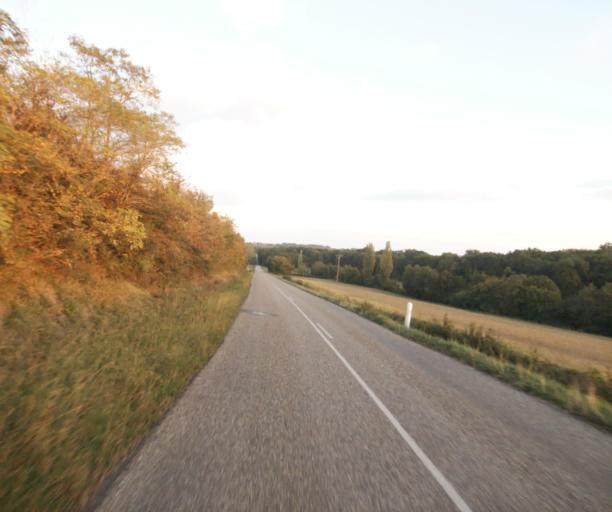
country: FR
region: Midi-Pyrenees
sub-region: Departement du Gers
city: Vic-Fezensac
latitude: 43.7944
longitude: 0.2479
